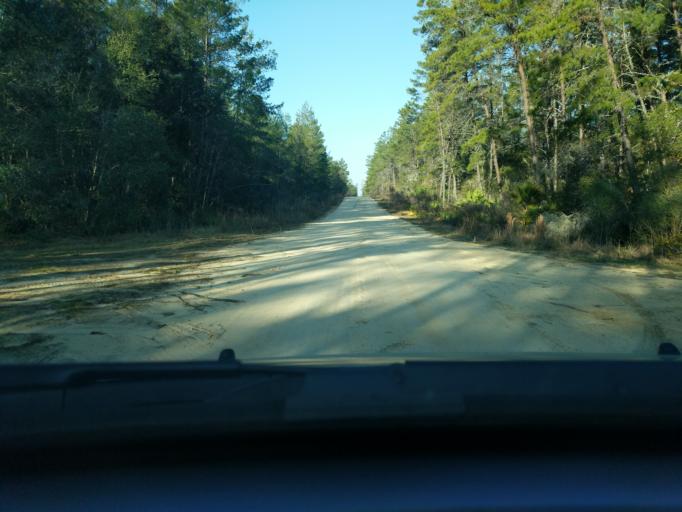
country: US
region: Florida
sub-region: Marion County
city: Silver Springs Shores
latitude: 29.2263
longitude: -81.7890
